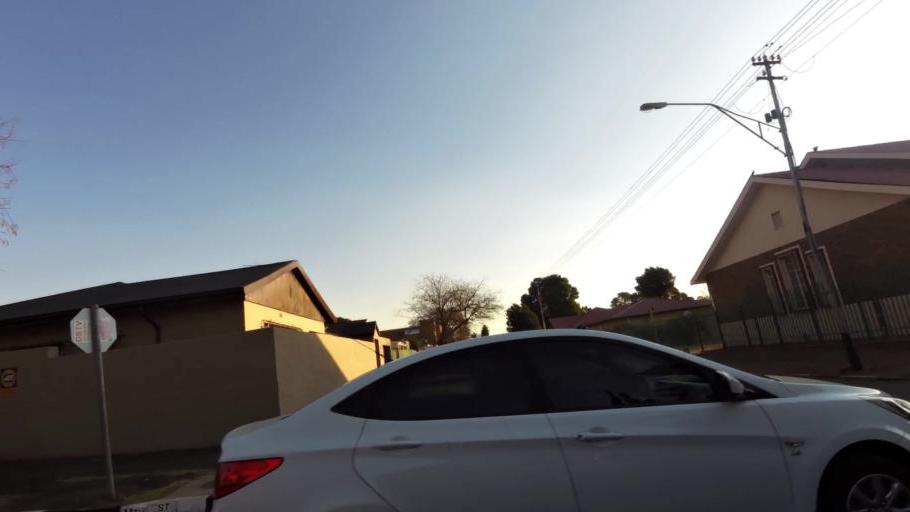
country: ZA
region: Gauteng
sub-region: City of Johannesburg Metropolitan Municipality
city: Johannesburg
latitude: -26.1701
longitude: 27.9632
